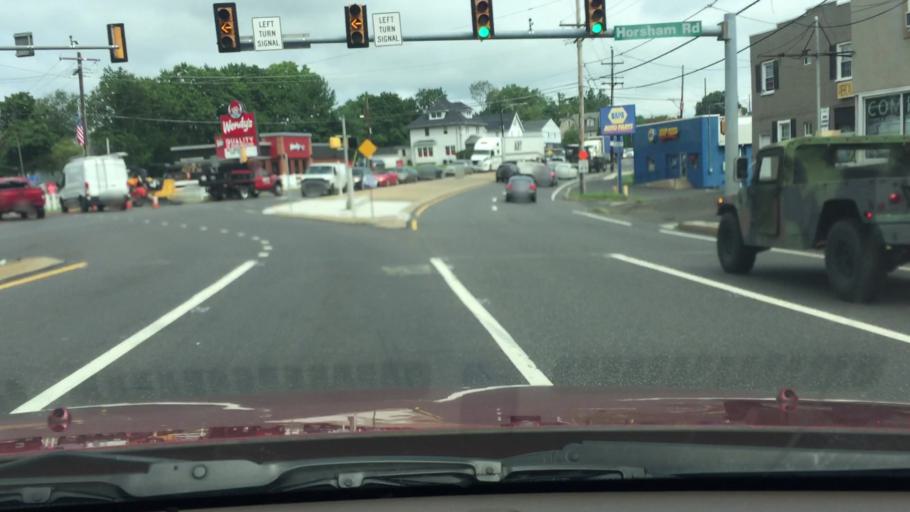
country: US
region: Pennsylvania
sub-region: Montgomery County
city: Horsham
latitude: 40.1794
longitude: -75.1299
